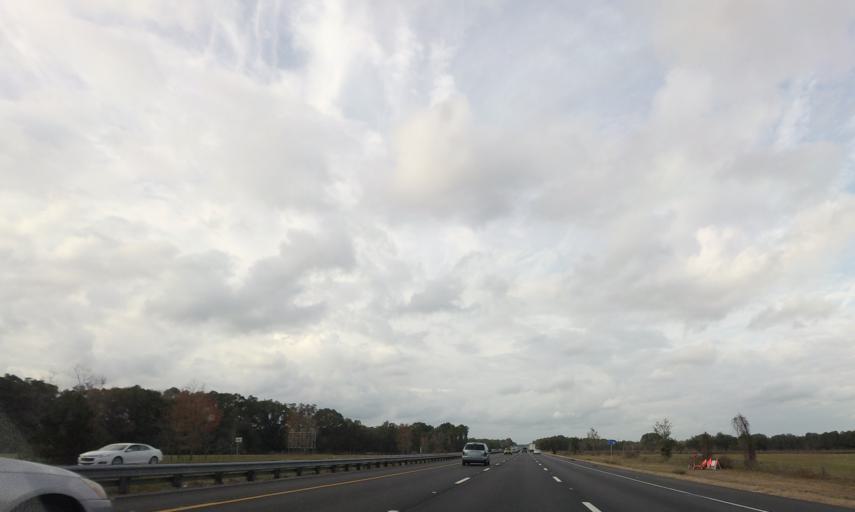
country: US
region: Florida
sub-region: Alachua County
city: High Springs
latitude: 29.9062
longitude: -82.5496
